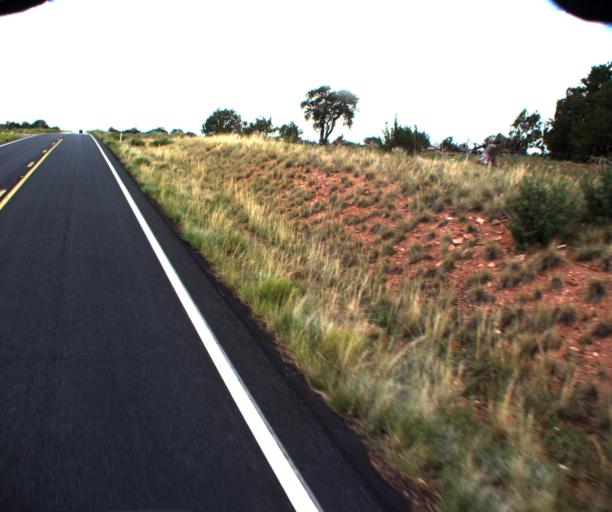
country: US
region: Arizona
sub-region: Coconino County
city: Parks
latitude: 35.6065
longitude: -112.0484
